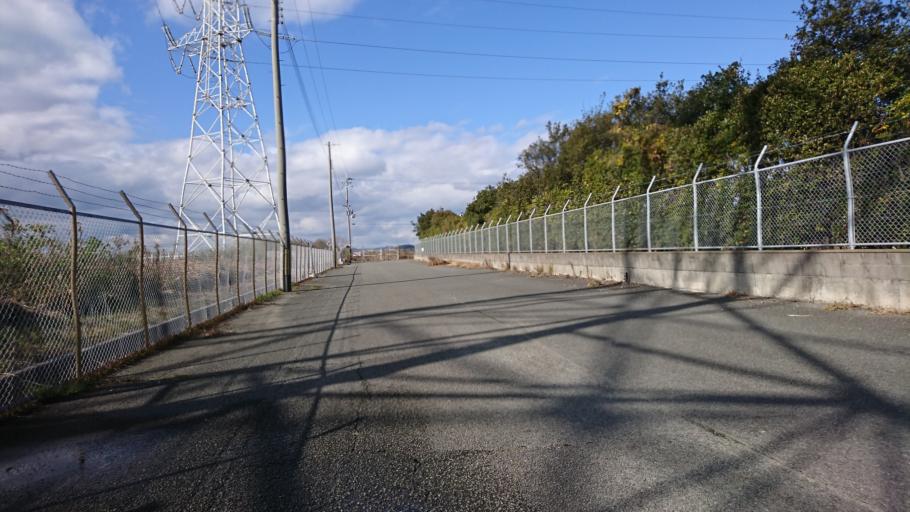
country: JP
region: Hyogo
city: Shirahamacho-usazakiminami
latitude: 34.7511
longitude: 134.7646
